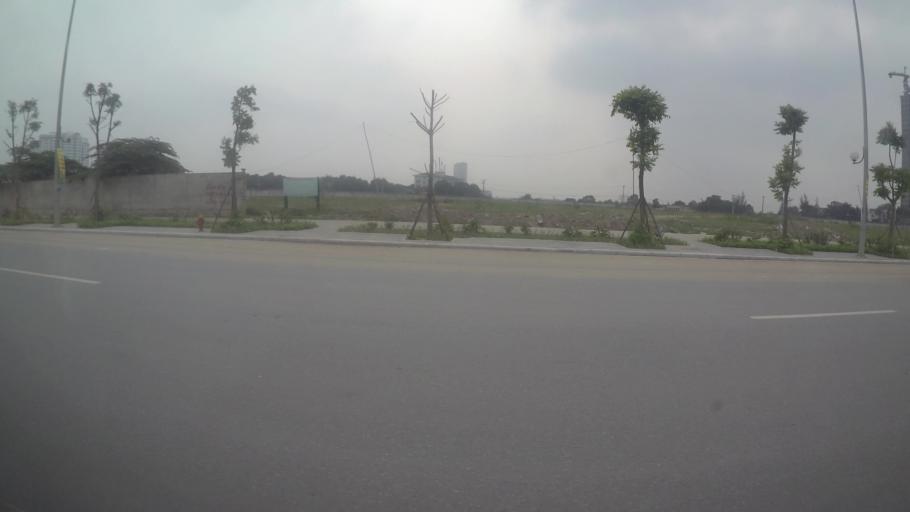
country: VN
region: Ha Noi
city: Cau Dien
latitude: 21.0457
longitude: 105.7364
